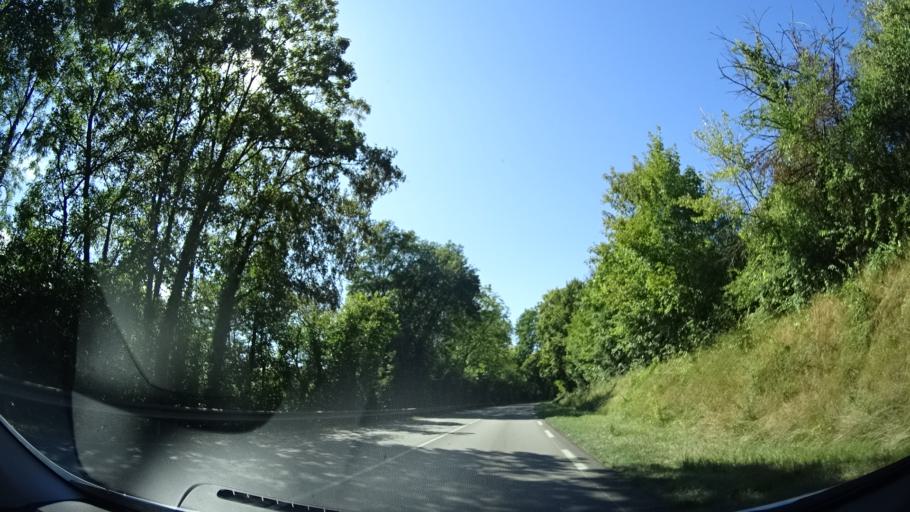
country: FR
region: Bourgogne
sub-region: Departement de l'Yonne
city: Charny
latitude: 47.9328
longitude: 3.1005
